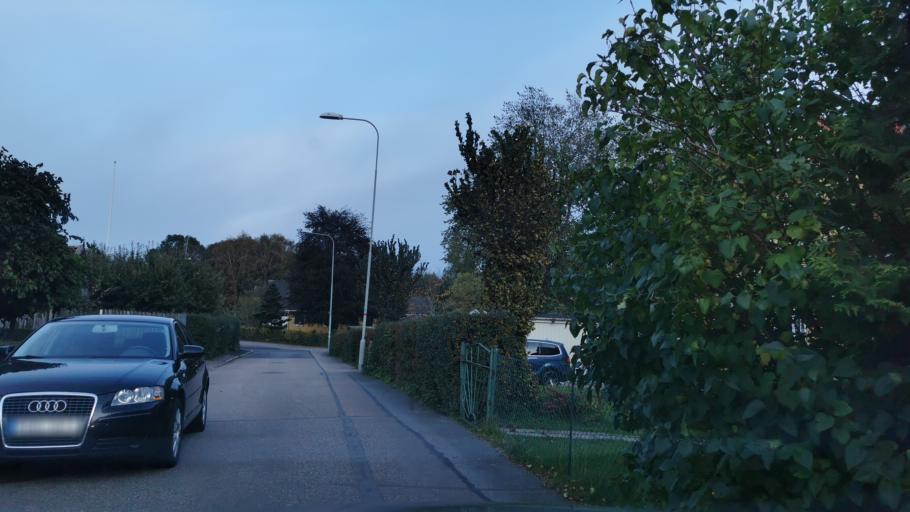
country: SE
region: Vaestra Goetaland
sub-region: Goteborg
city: Eriksbo
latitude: 57.7335
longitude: 12.0445
